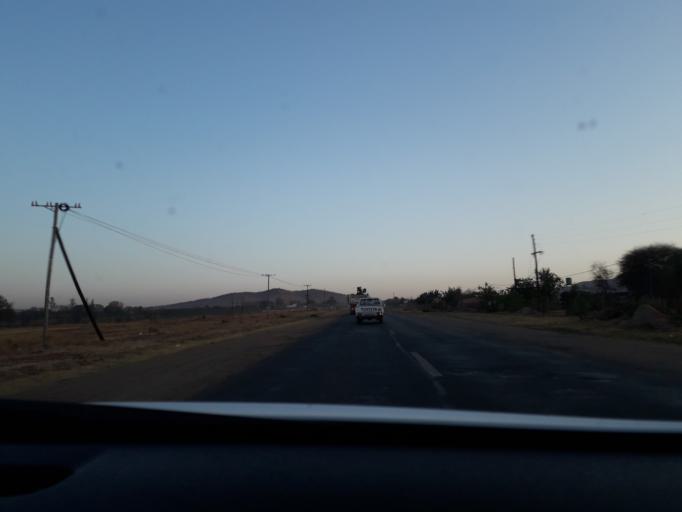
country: ZA
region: Limpopo
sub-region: Waterberg District Municipality
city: Mokopane
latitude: -24.0836
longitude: 28.9704
